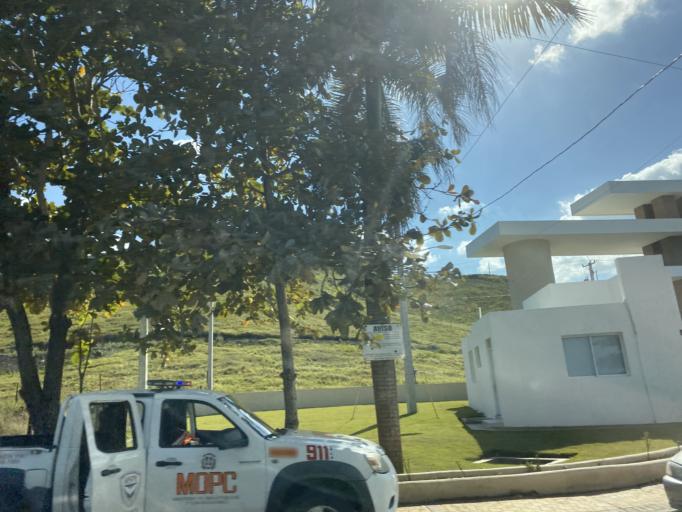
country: DO
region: Espaillat
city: Gaspar Hernandez
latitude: 19.6407
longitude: -70.2571
